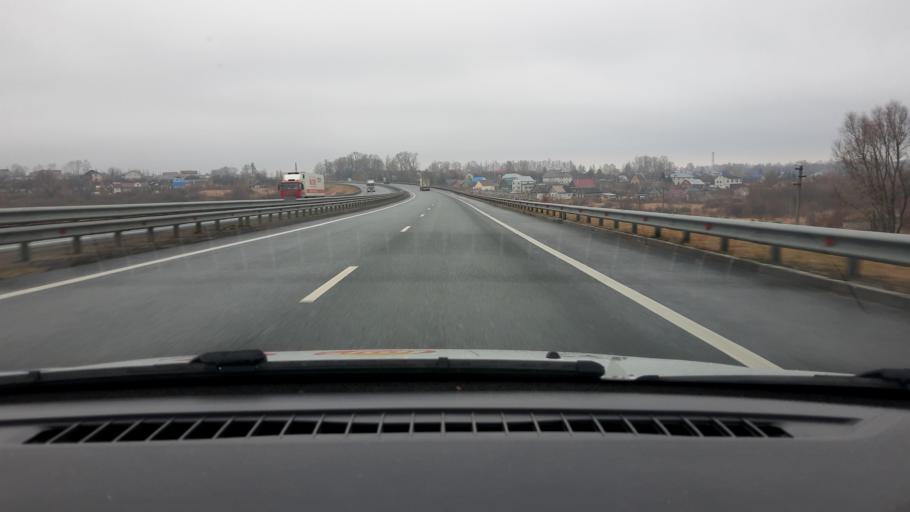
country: RU
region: Nizjnij Novgorod
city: Burevestnik
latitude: 56.1615
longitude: 43.7494
